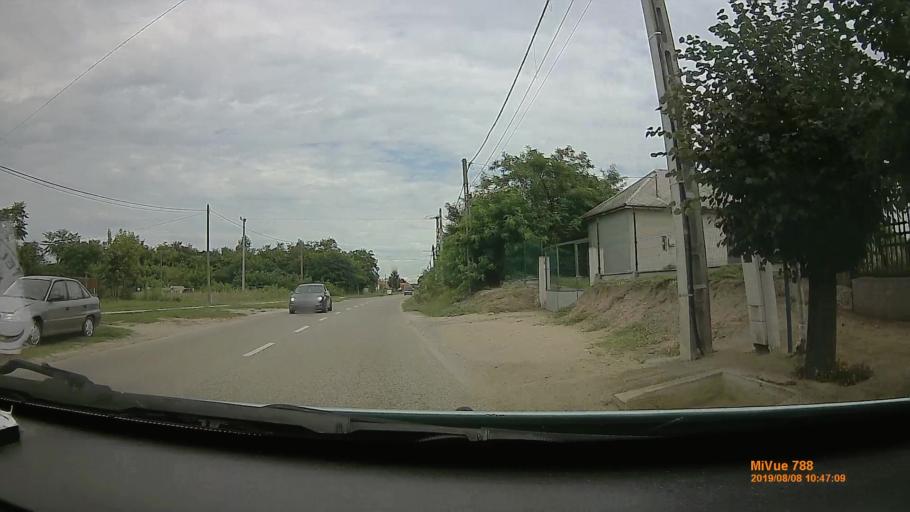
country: HU
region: Szabolcs-Szatmar-Bereg
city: Balkany
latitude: 47.7591
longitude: 21.8624
